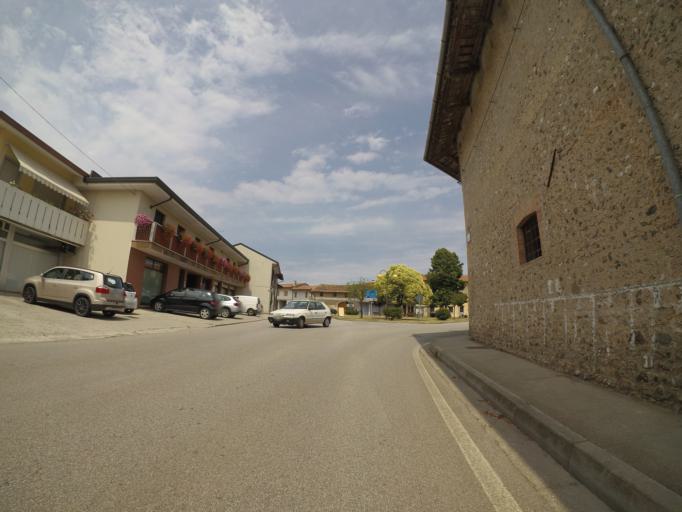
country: IT
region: Friuli Venezia Giulia
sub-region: Provincia di Udine
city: Sedegliano
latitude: 46.0004
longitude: 12.9977
